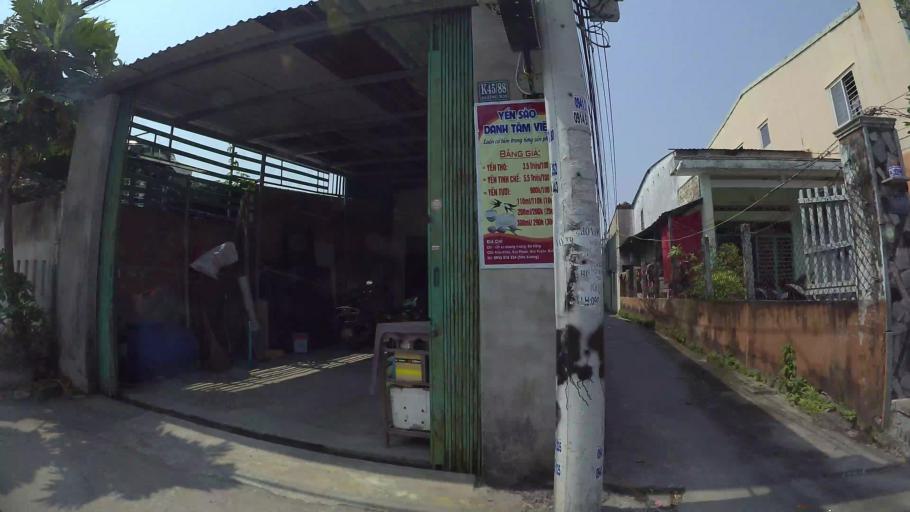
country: VN
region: Da Nang
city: Ngu Hanh Son
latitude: 16.0210
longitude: 108.2488
